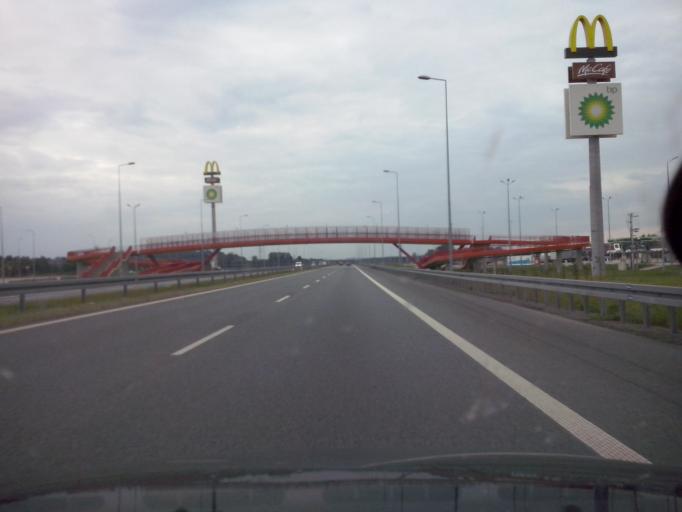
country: PL
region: Lesser Poland Voivodeship
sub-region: Powiat bochenski
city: Stanislawice
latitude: 49.9886
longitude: 20.3421
